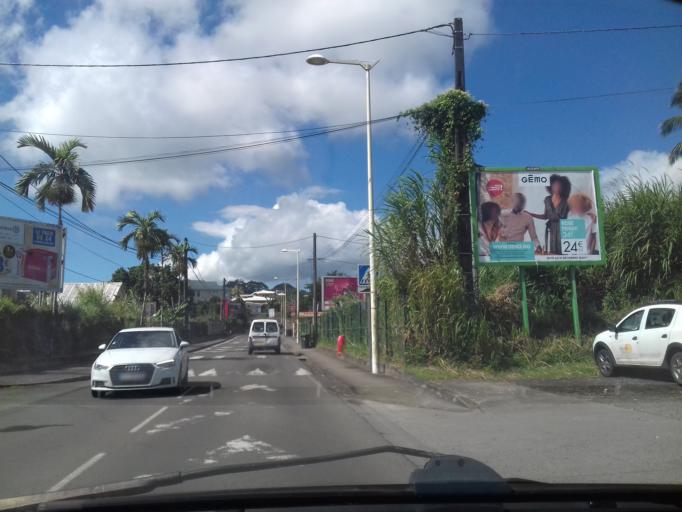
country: MQ
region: Martinique
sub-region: Martinique
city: Saint-Joseph
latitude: 14.6735
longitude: -61.0291
